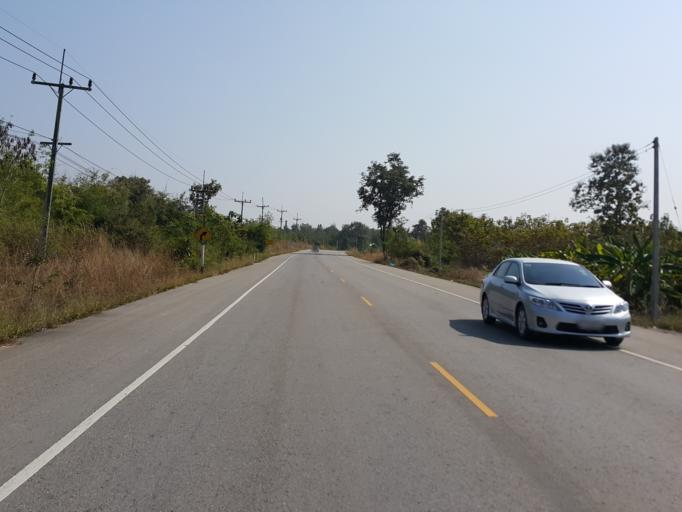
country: TH
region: Lampang
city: Mueang Pan
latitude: 18.9390
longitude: 99.6104
